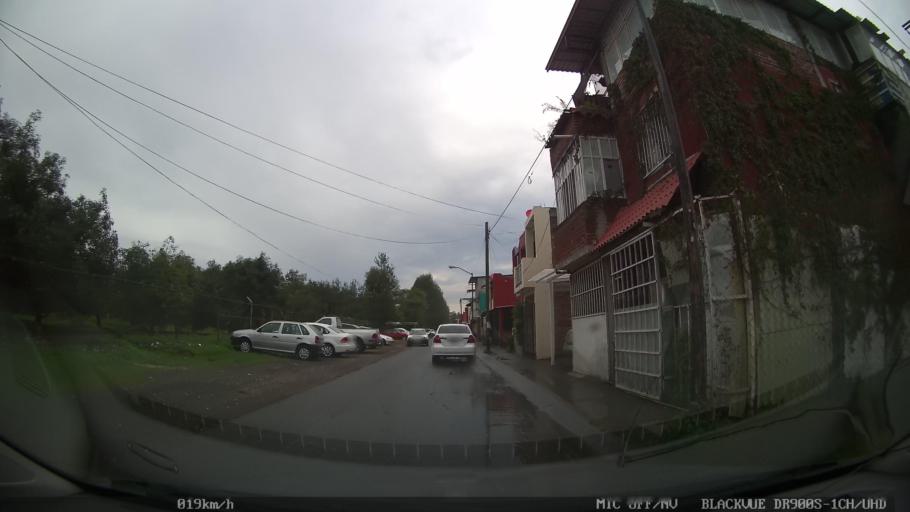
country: MX
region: Michoacan
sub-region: Uruapan
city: Santa Rosa (Santa Barbara)
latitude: 19.4009
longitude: -102.0284
